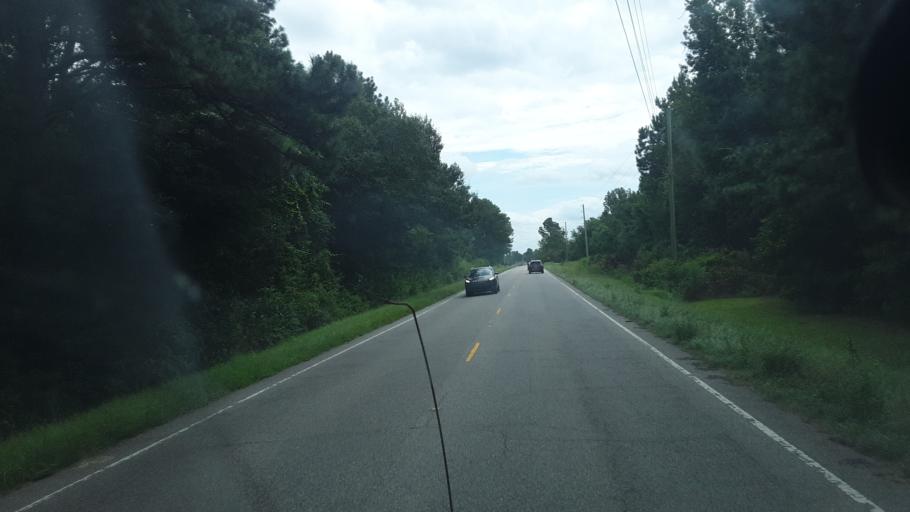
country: US
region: North Carolina
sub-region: Robeson County
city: Maxton
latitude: 34.6613
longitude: -79.3890
